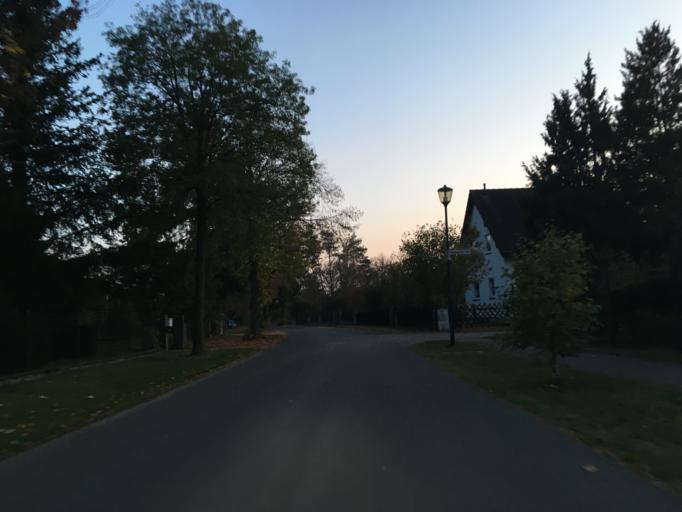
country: DE
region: Brandenburg
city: Birkenwerder
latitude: 52.6837
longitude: 13.3207
